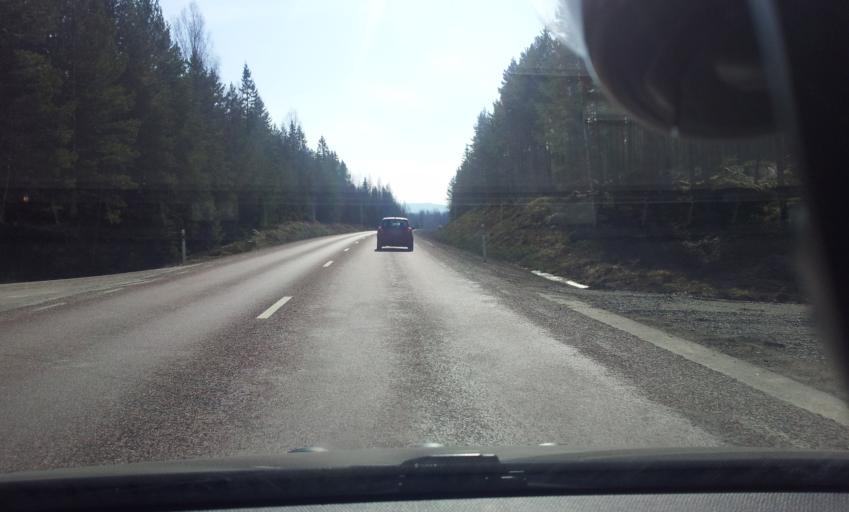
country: SE
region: Gaevleborg
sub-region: Ljusdals Kommun
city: Jaervsoe
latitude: 61.7706
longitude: 16.1549
